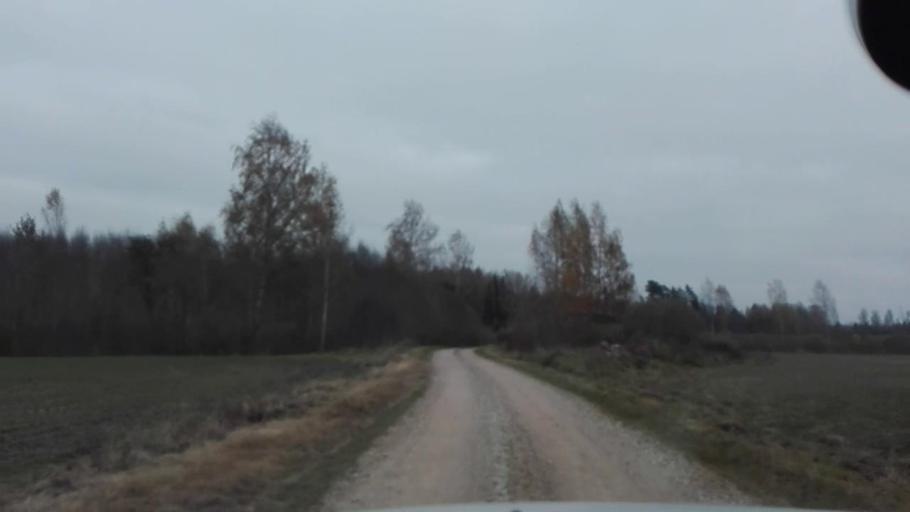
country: EE
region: Jogevamaa
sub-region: Poltsamaa linn
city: Poltsamaa
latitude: 58.5063
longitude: 25.9693
